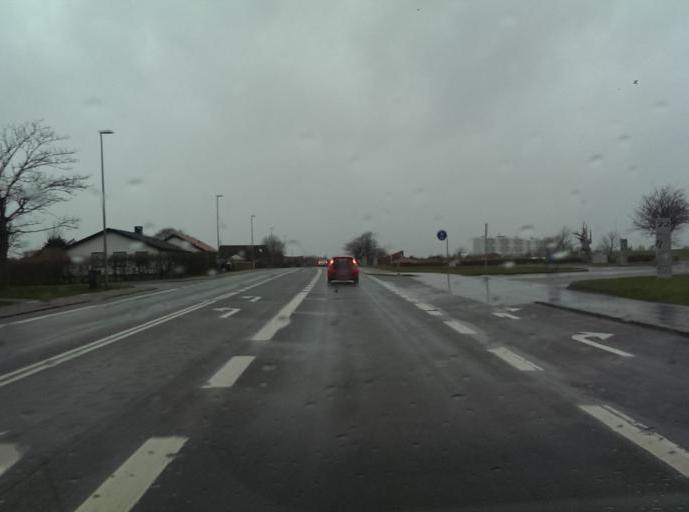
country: DK
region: South Denmark
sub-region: Esbjerg Kommune
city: Esbjerg
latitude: 55.4910
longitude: 8.4566
